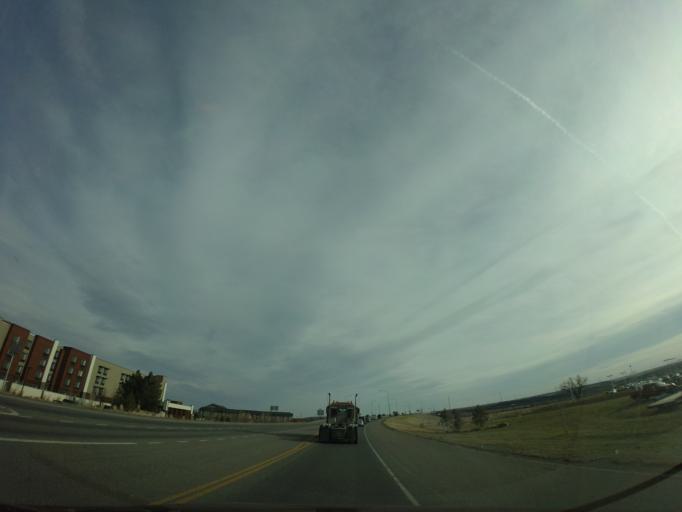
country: US
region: Montana
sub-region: Yellowstone County
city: Billings
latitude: 45.7350
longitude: -108.6081
